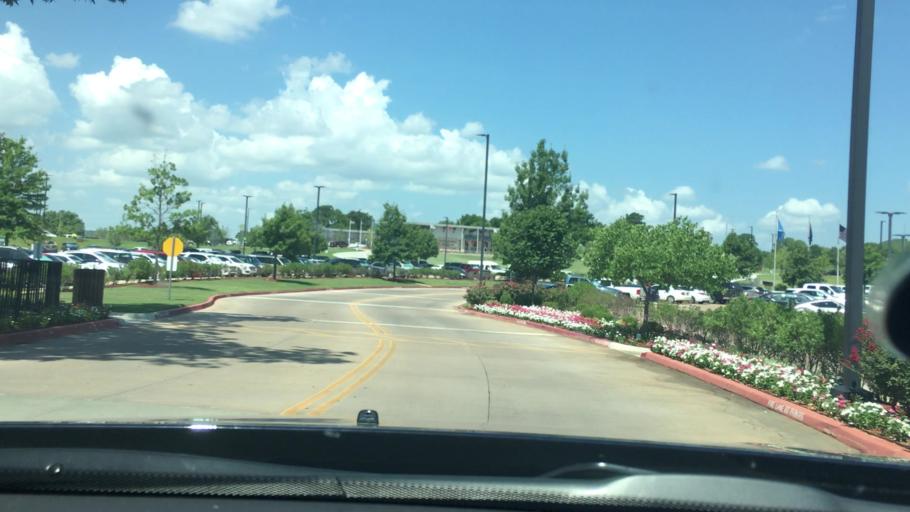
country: US
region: Oklahoma
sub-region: Pontotoc County
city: Ada
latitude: 34.7312
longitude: -96.6466
